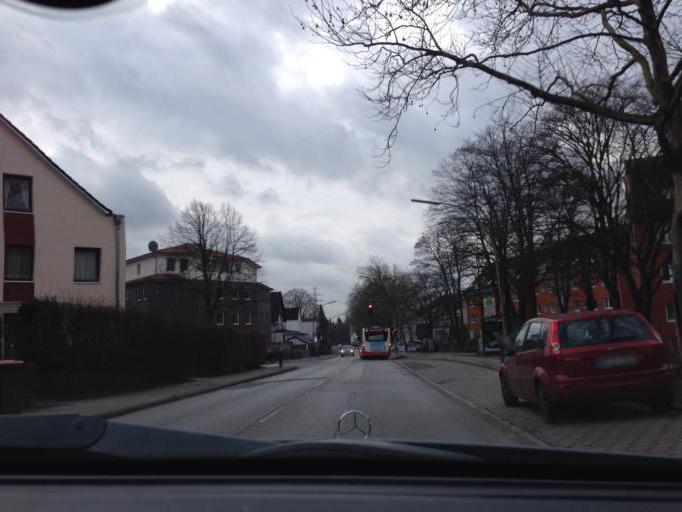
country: DE
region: Hamburg
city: Farmsen-Berne
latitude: 53.6039
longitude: 10.1310
